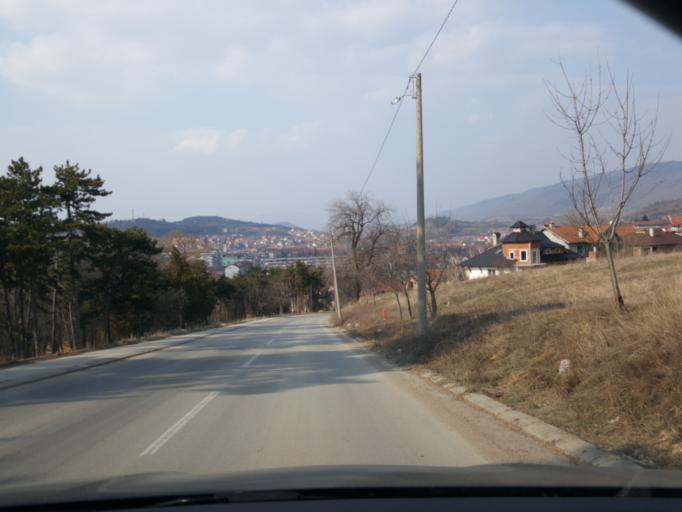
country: RS
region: Central Serbia
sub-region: Nisavski Okrug
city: Aleksinac
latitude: 43.5343
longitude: 21.7133
